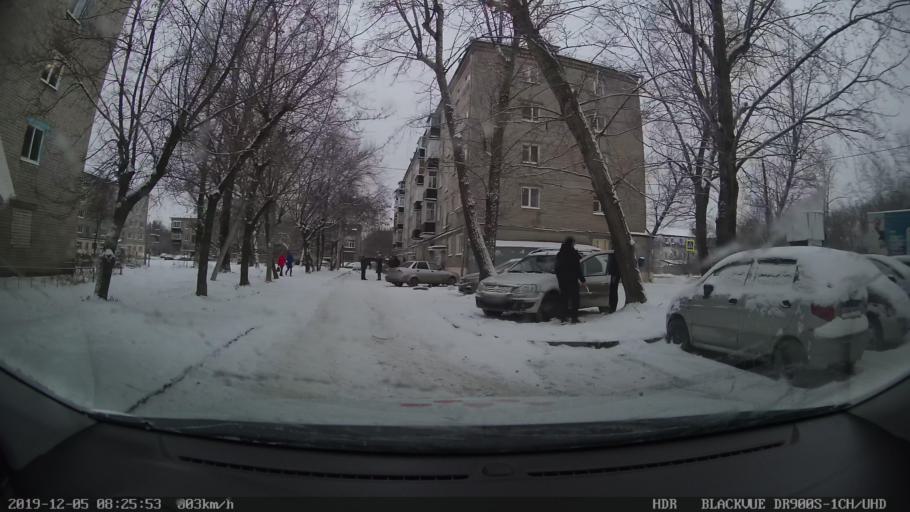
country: RU
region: Tatarstan
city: Staroye Arakchino
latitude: 55.8782
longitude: 49.0236
